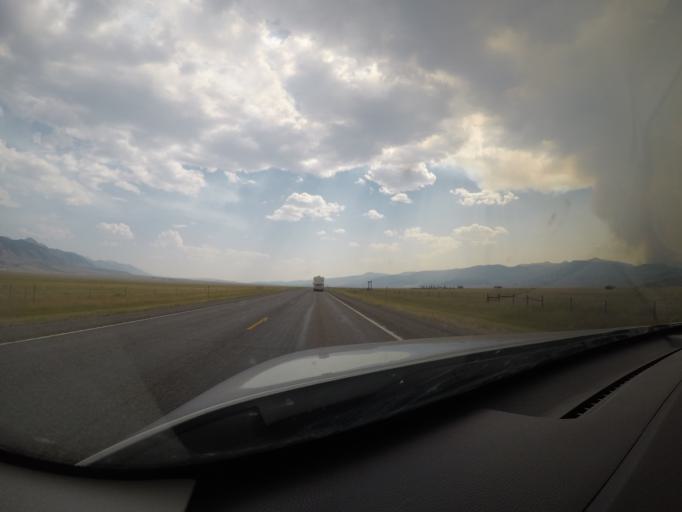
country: US
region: Montana
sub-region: Gallatin County
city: Big Sky
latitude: 45.0660
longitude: -111.6462
